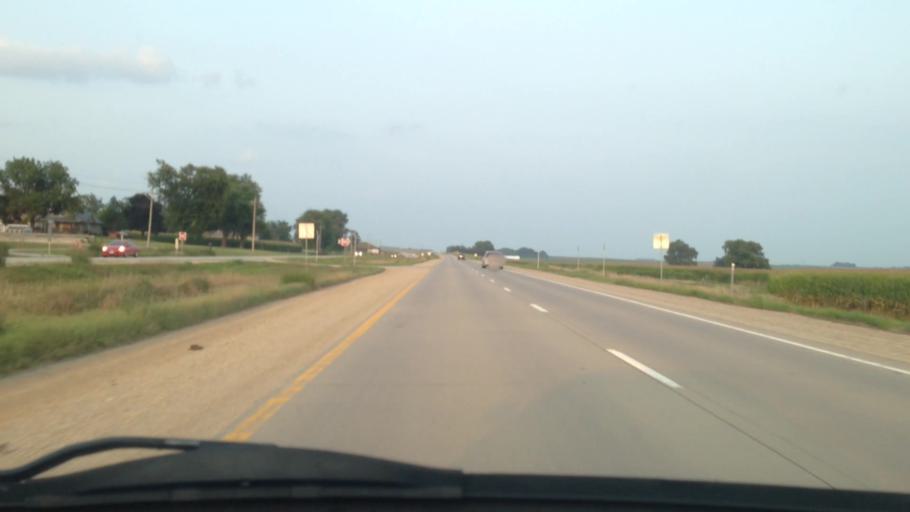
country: US
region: Iowa
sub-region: Benton County
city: Atkins
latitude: 41.9634
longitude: -91.8689
